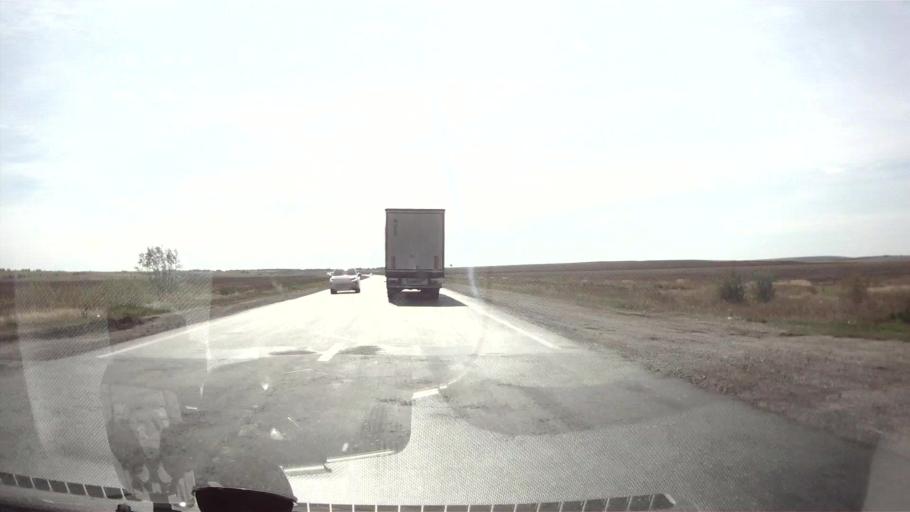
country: RU
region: Samara
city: Varlamovo
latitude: 53.0302
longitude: 48.3348
